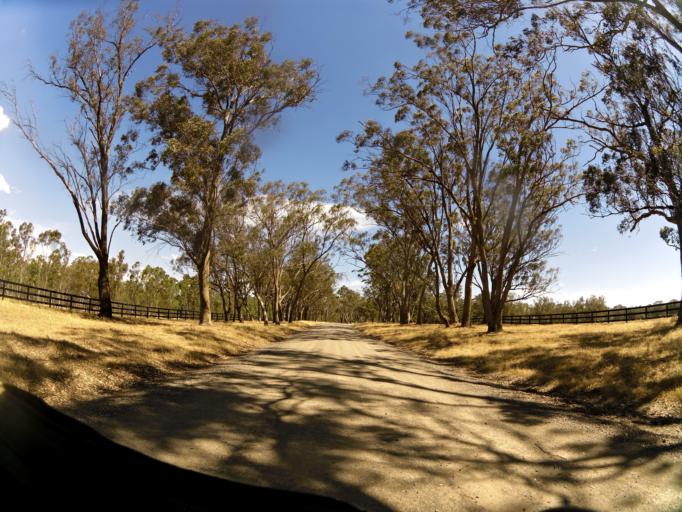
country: AU
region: Victoria
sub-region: Campaspe
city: Kyabram
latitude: -36.8275
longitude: 145.0780
